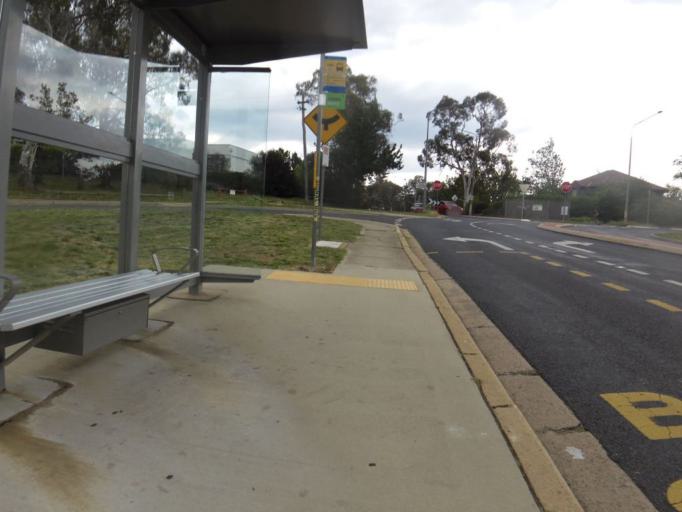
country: AU
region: Australian Capital Territory
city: Forrest
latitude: -35.3430
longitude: 149.1385
